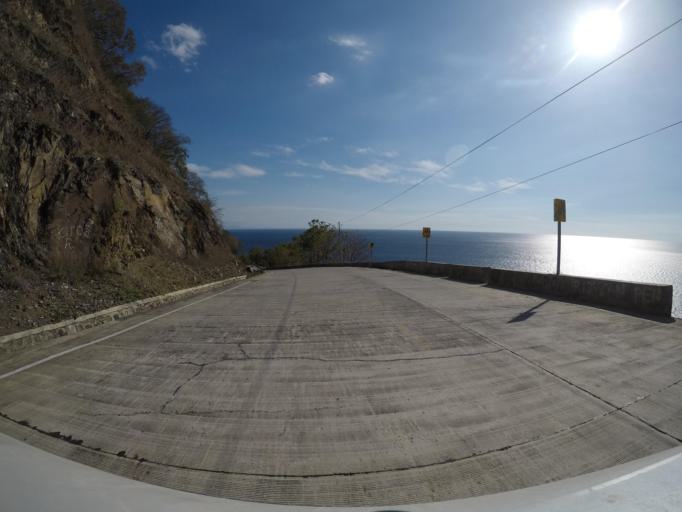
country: TL
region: Liquica
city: Maubara
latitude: -8.6655
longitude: 125.1111
